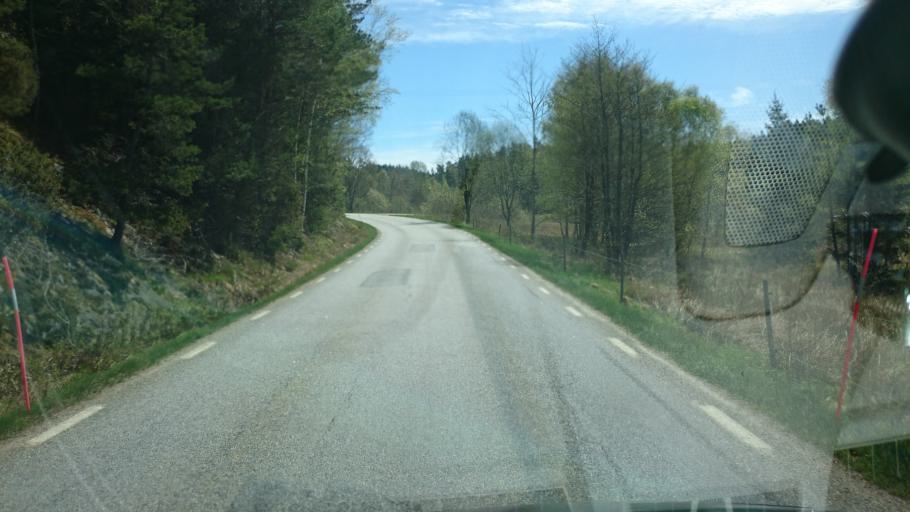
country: SE
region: Vaestra Goetaland
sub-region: Munkedals Kommun
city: Munkedal
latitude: 58.3722
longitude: 11.6883
